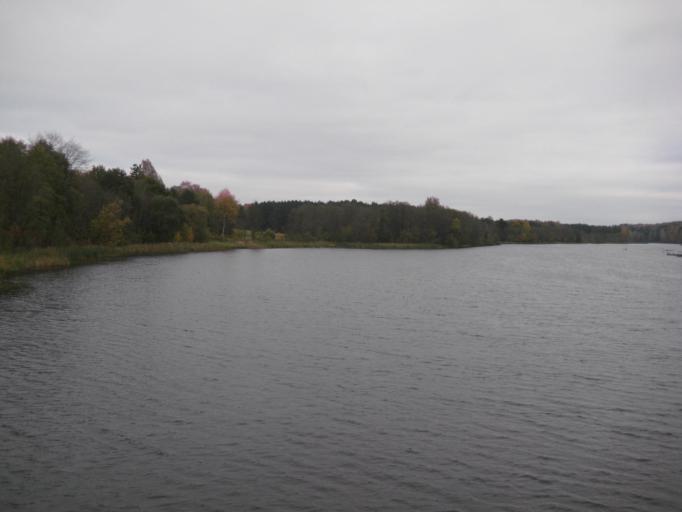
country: LT
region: Utenos apskritis
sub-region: Anyksciai
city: Anyksciai
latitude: 55.4390
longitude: 24.9415
